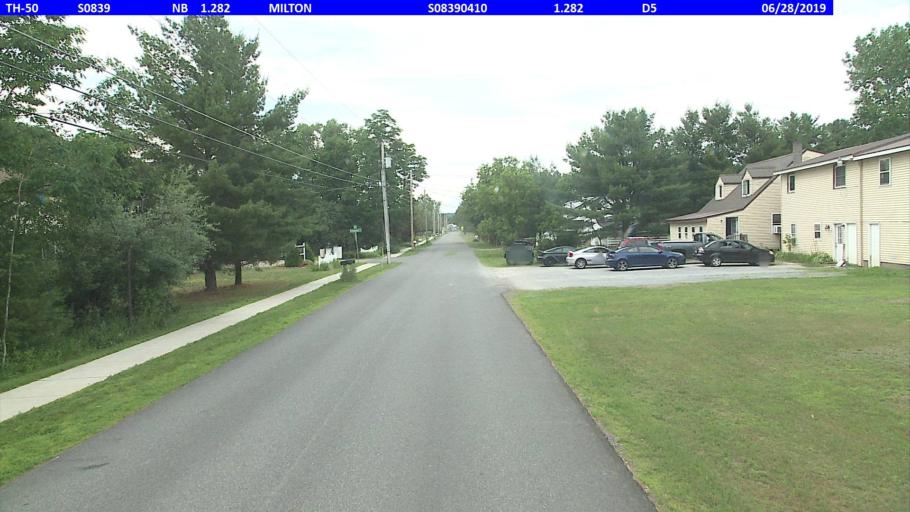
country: US
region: Vermont
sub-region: Chittenden County
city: Milton
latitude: 44.6219
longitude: -73.1116
